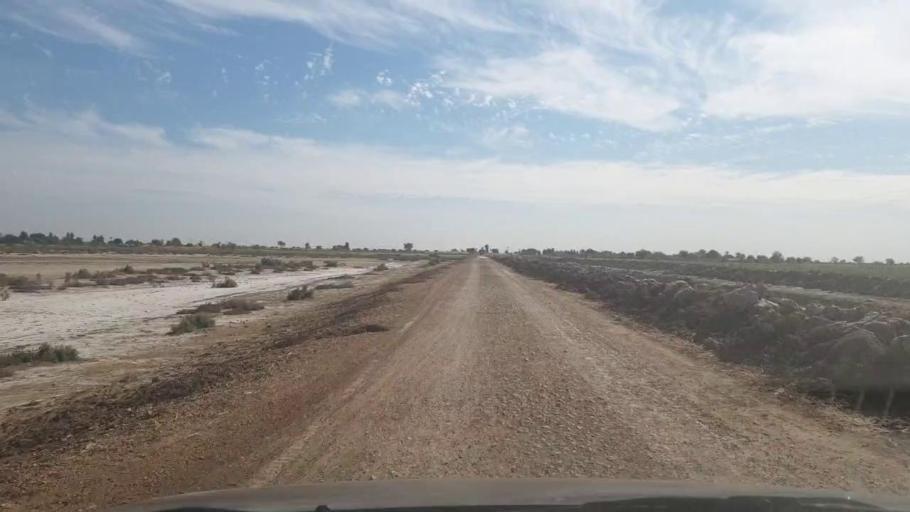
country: PK
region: Sindh
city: Mirwah Gorchani
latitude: 25.4246
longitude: 69.2007
